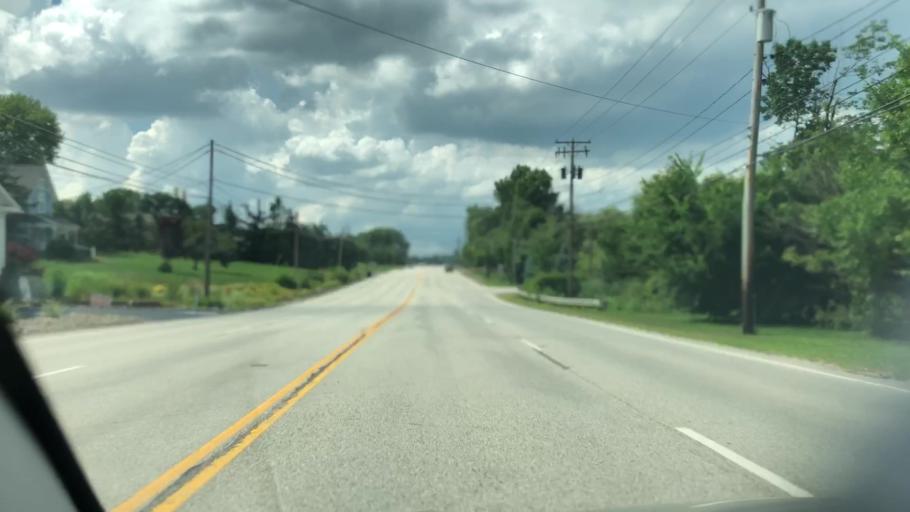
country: US
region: Ohio
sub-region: Summit County
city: Montrose-Ghent
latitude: 41.1462
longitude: -81.6236
